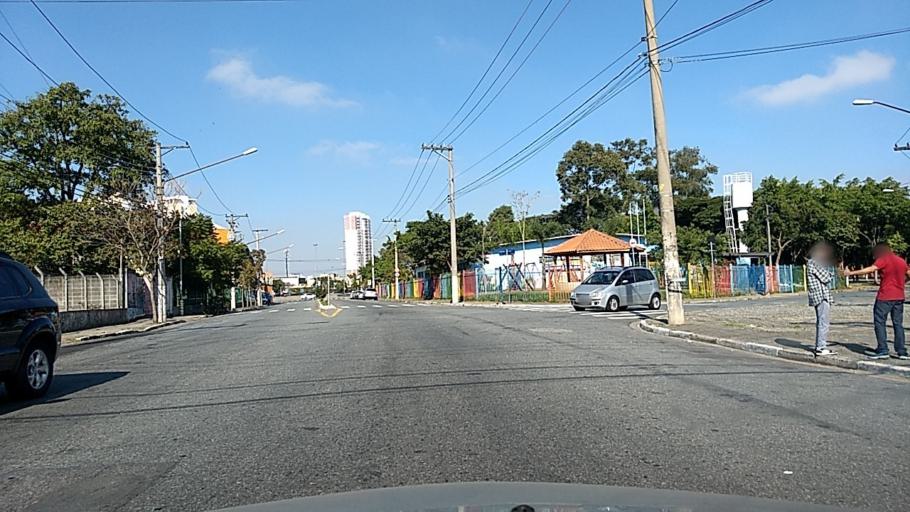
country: BR
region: Sao Paulo
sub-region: Sao Paulo
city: Sao Paulo
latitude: -23.5207
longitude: -46.6071
